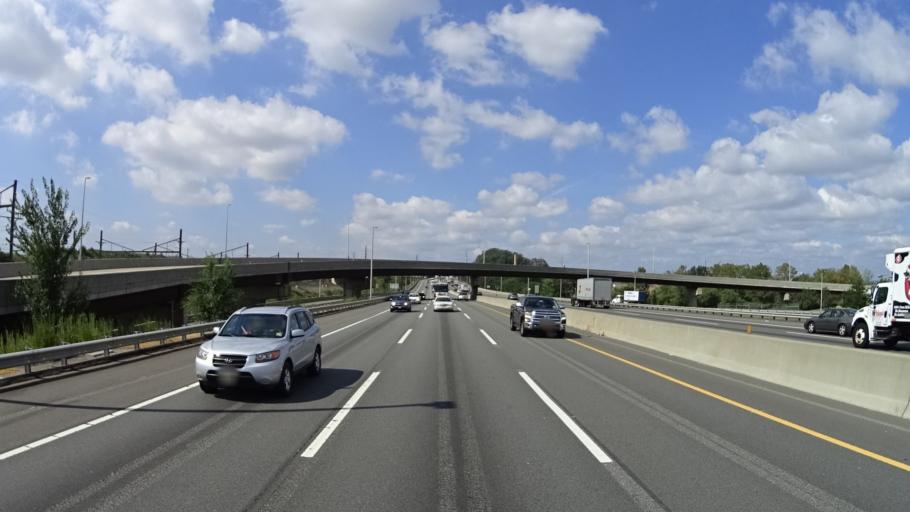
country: US
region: New Jersey
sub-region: Hudson County
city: Jersey City
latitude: 40.7612
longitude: -74.0779
